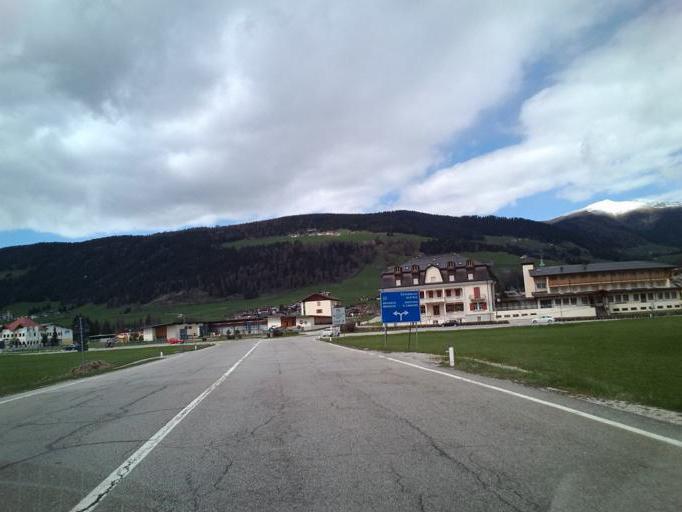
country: IT
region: Trentino-Alto Adige
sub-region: Bolzano
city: Dobbiaco
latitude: 46.7279
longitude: 12.2205
